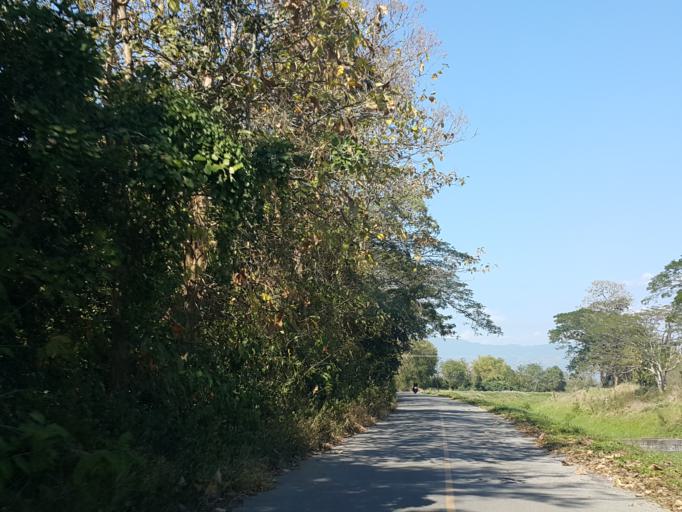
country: TH
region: Chiang Mai
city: Mae Taeng
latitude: 19.0856
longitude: 98.9513
